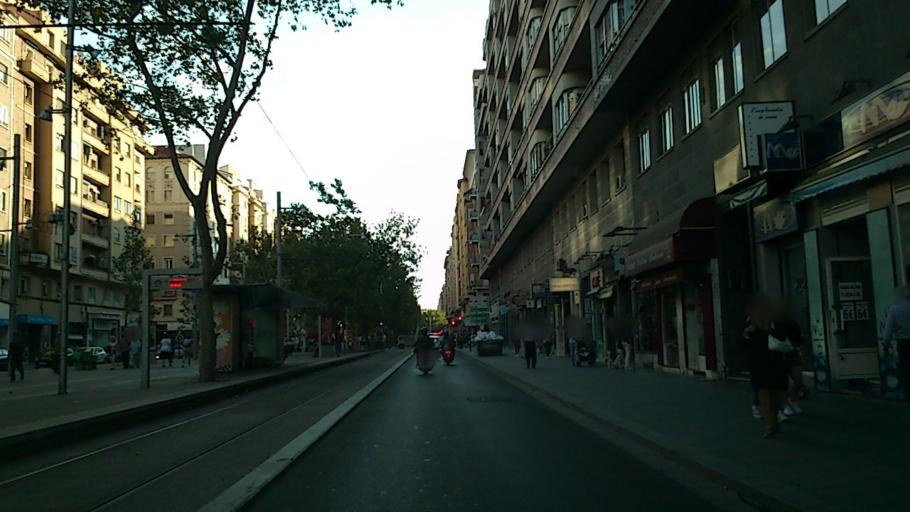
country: ES
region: Aragon
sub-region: Provincia de Zaragoza
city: Delicias
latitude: 41.6440
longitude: -0.8922
